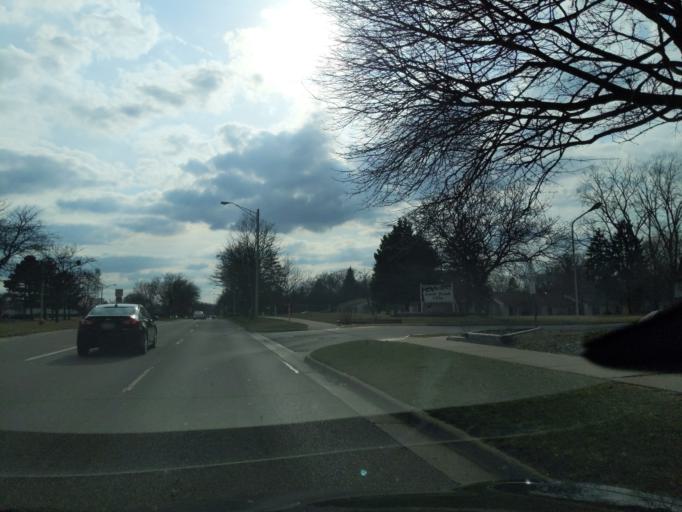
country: US
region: Michigan
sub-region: Ingham County
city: Holt
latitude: 42.6640
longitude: -84.5464
